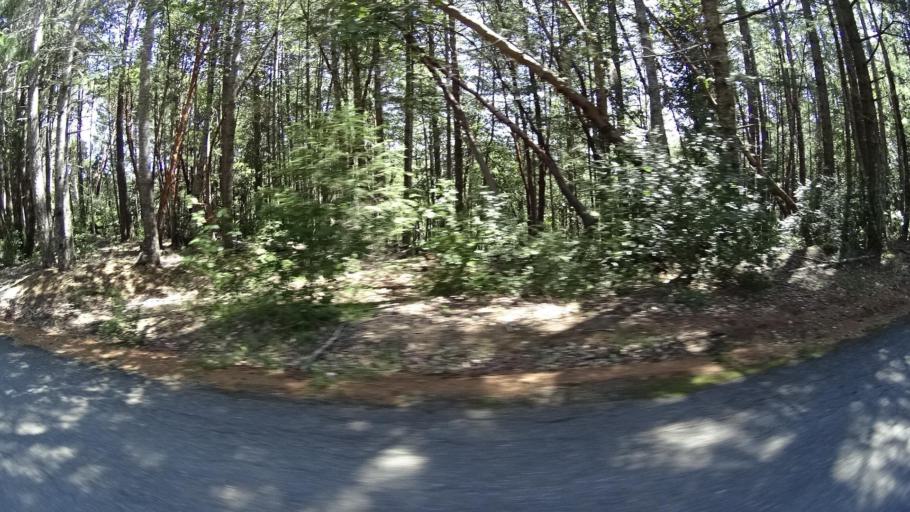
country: US
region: California
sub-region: Humboldt County
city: Redway
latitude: 40.1946
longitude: -124.0954
